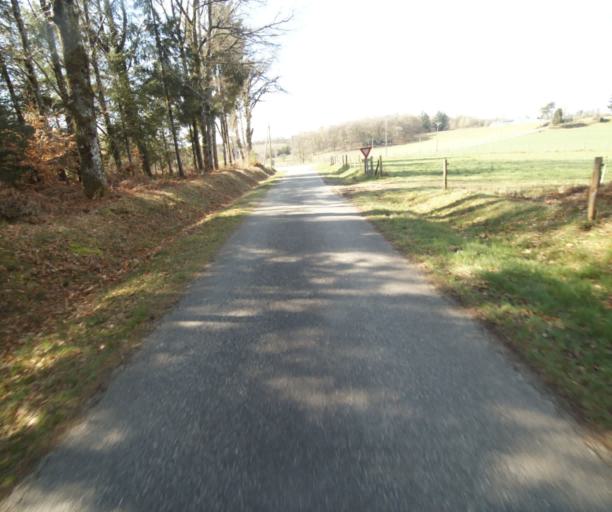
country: FR
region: Limousin
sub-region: Departement de la Correze
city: Laguenne
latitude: 45.2389
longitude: 1.9124
